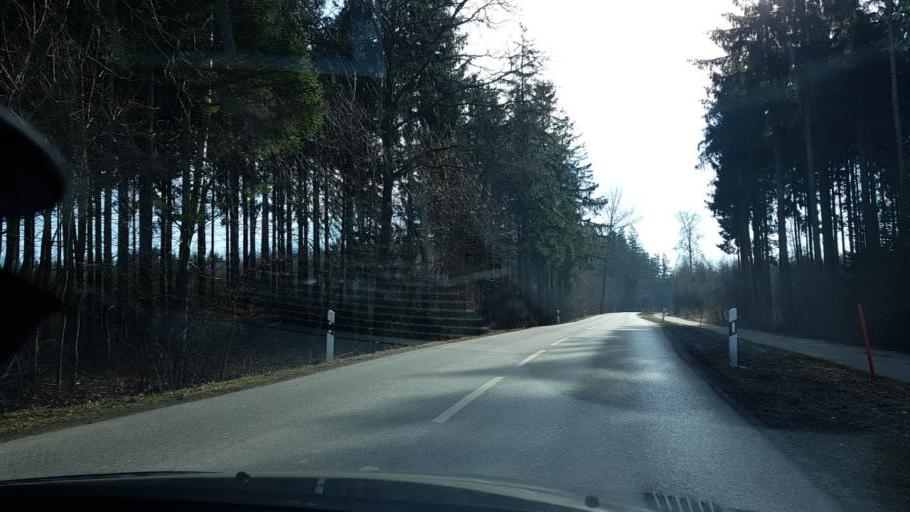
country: DE
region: Bavaria
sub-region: Upper Bavaria
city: Oberschweinbach
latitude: 48.2336
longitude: 11.1653
